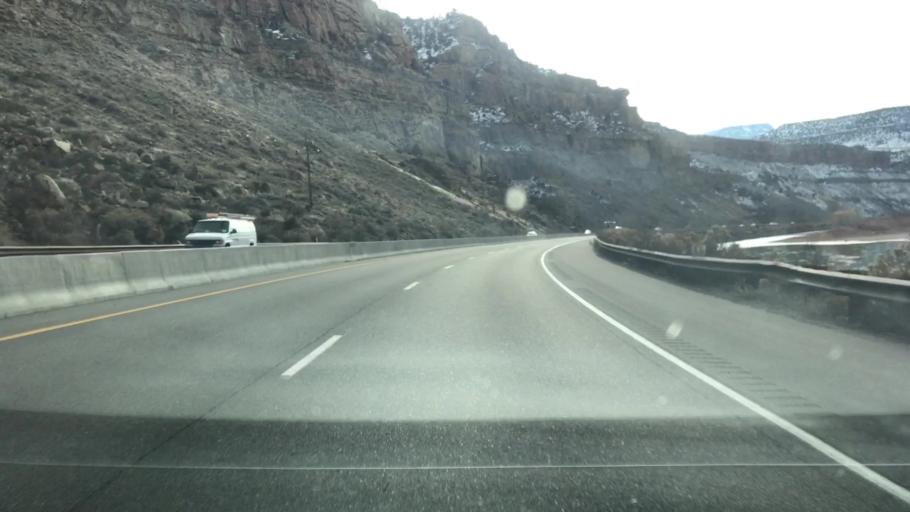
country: US
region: Colorado
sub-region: Mesa County
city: Palisade
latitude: 39.2258
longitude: -108.2574
